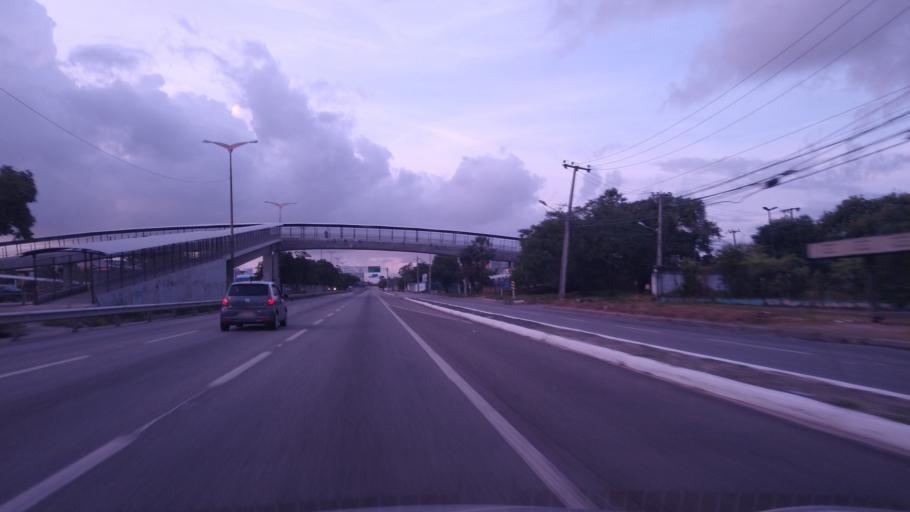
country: BR
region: Ceara
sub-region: Fortaleza
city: Fortaleza
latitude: -3.7931
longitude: -38.5085
